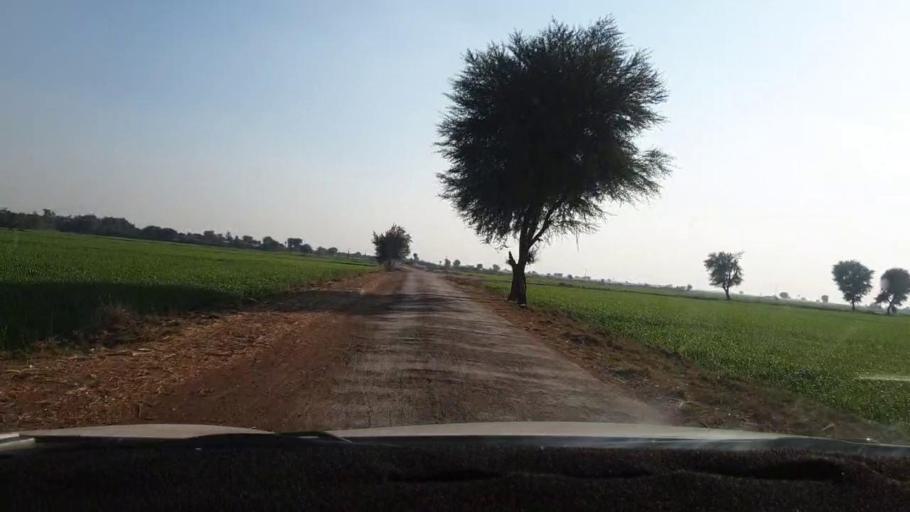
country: PK
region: Sindh
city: Berani
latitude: 25.7669
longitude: 68.7685
